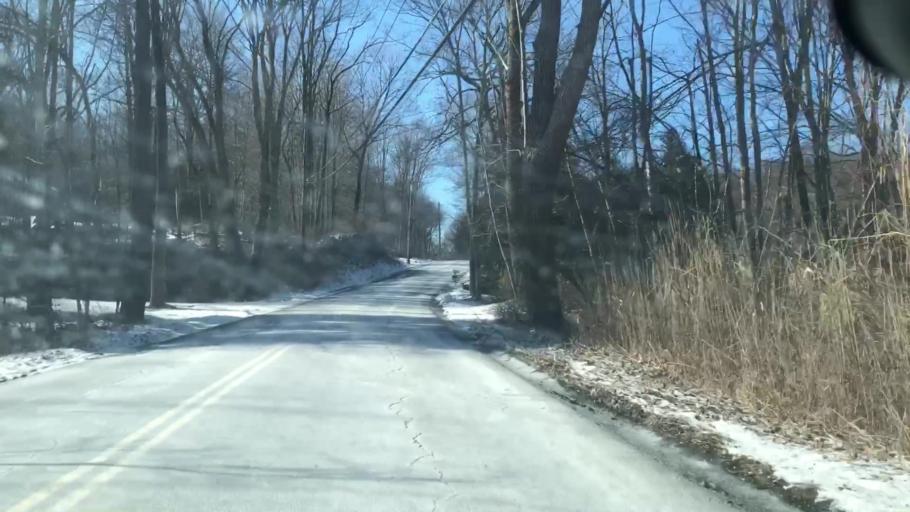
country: US
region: New York
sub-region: Putnam County
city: Carmel Hamlet
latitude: 41.3870
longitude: -73.6934
